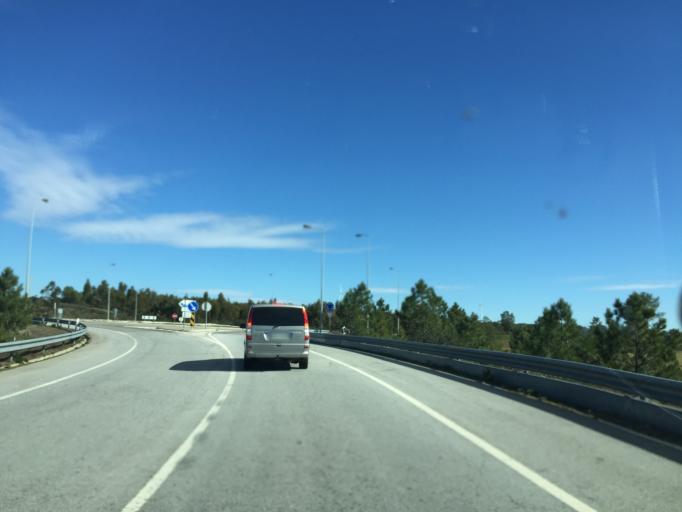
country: PT
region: Castelo Branco
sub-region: Castelo Branco
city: Castelo Branco
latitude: 39.7575
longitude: -7.6059
